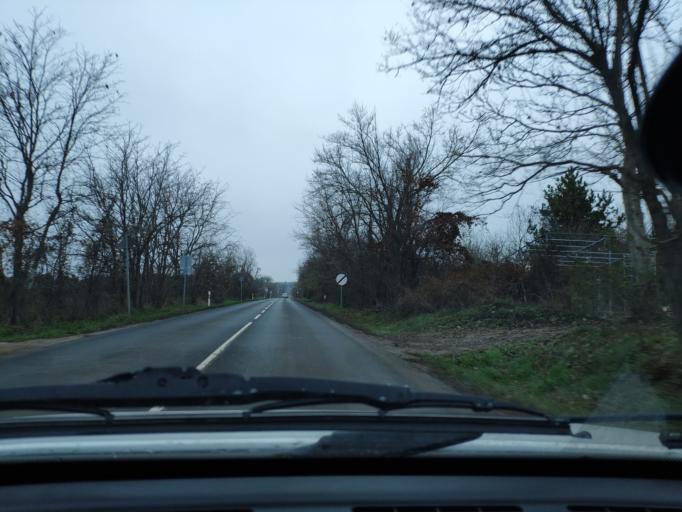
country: HU
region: Pest
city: Soskut
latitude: 47.4297
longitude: 18.8241
